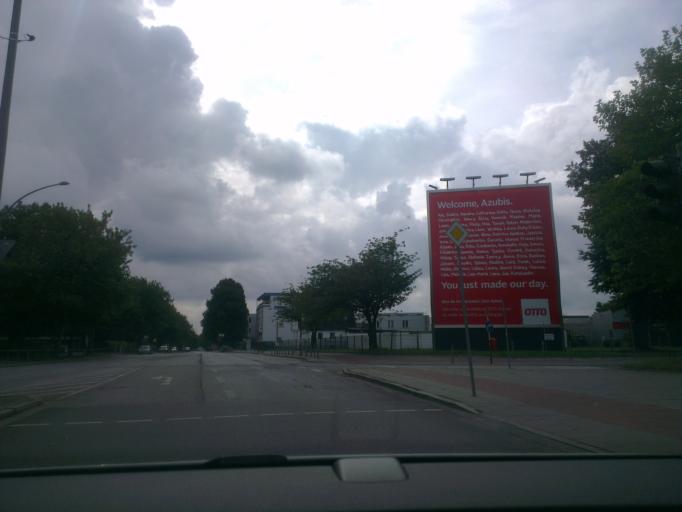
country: DE
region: Hamburg
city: Steilshoop
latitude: 53.6011
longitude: 10.0688
